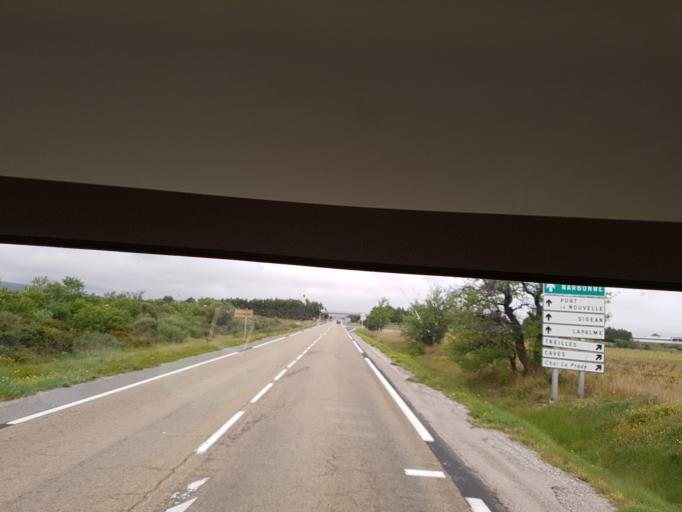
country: FR
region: Languedoc-Roussillon
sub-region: Departement de l'Aude
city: Leucate
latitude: 42.9291
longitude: 2.9934
